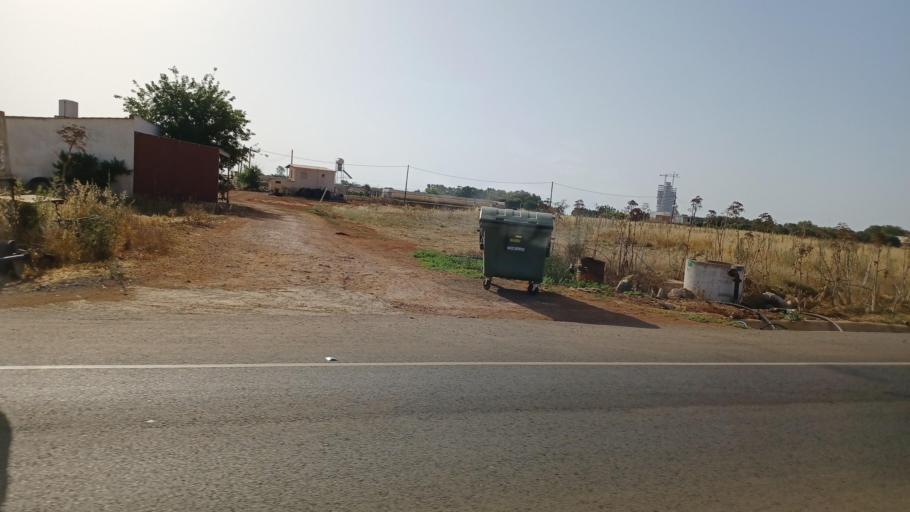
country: CY
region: Ammochostos
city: Liopetri
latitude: 34.9902
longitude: 33.9314
